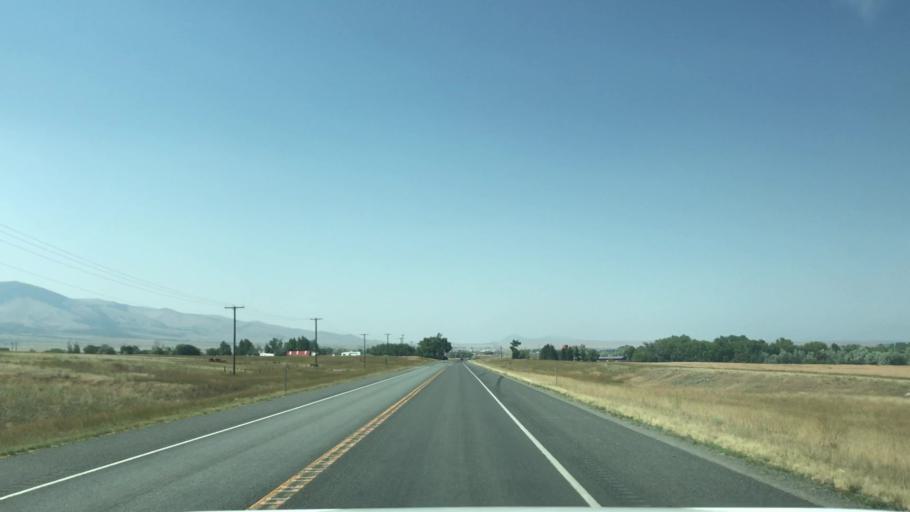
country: US
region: Montana
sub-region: Broadwater County
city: Townsend
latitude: 46.3581
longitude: -111.5470
